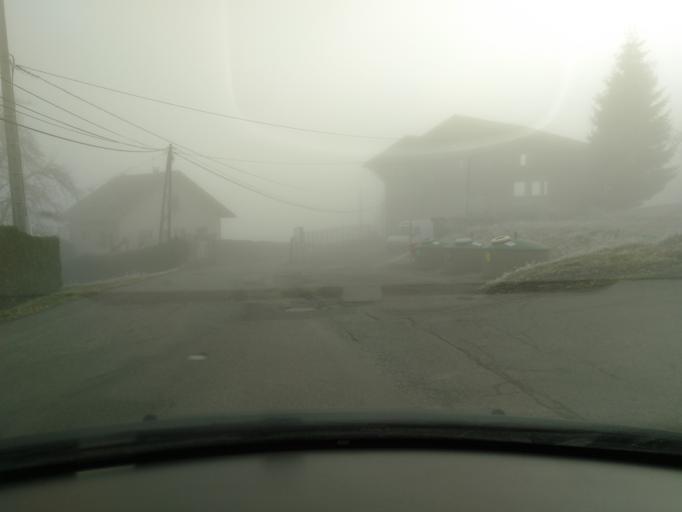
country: FR
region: Rhone-Alpes
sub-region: Departement de la Haute-Savoie
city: Sallanches
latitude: 45.9630
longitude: 6.6170
